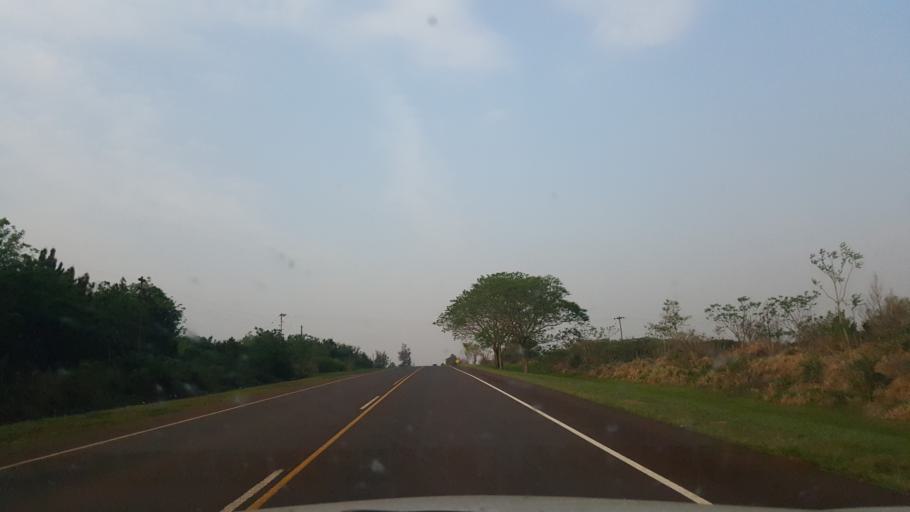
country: AR
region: Misiones
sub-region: Departamento de Capital
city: Posadas
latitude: -27.4265
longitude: -56.0010
